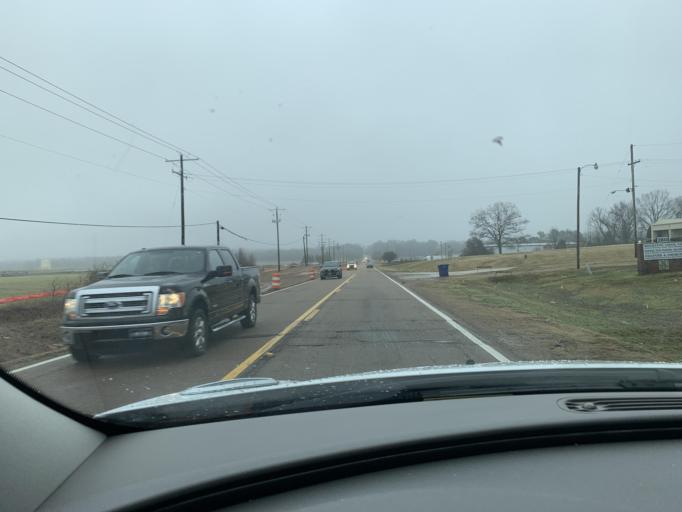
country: US
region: Mississippi
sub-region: De Soto County
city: Hernando
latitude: 34.8638
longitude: -89.9953
